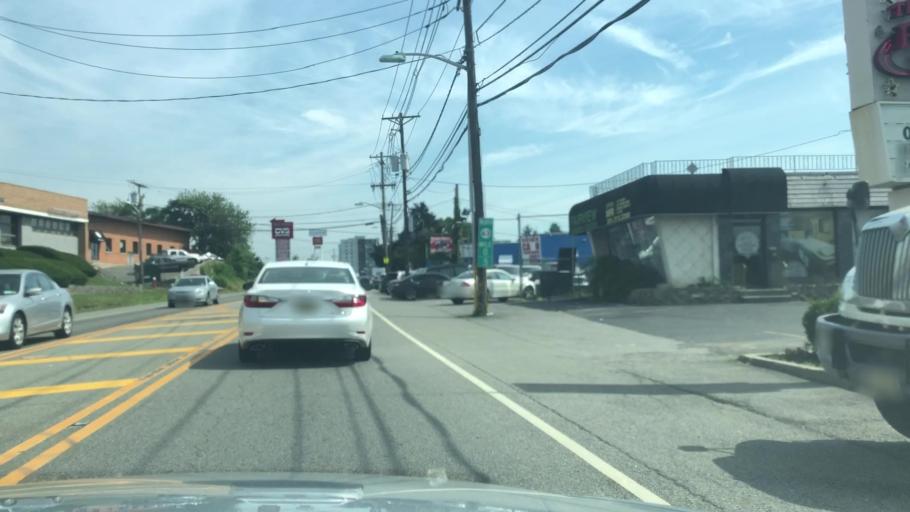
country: US
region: New Jersey
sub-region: Bergen County
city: Fairview
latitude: 40.8172
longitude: -74.0018
